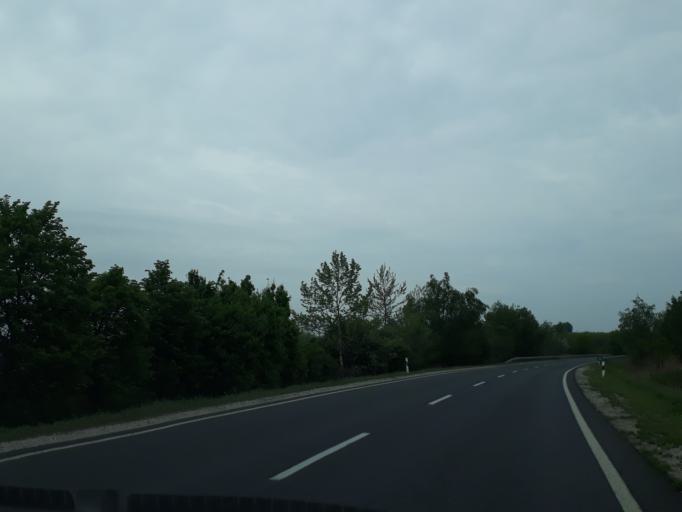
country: HU
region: Szabolcs-Szatmar-Bereg
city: Nyirtass
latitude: 48.0839
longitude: 21.9845
